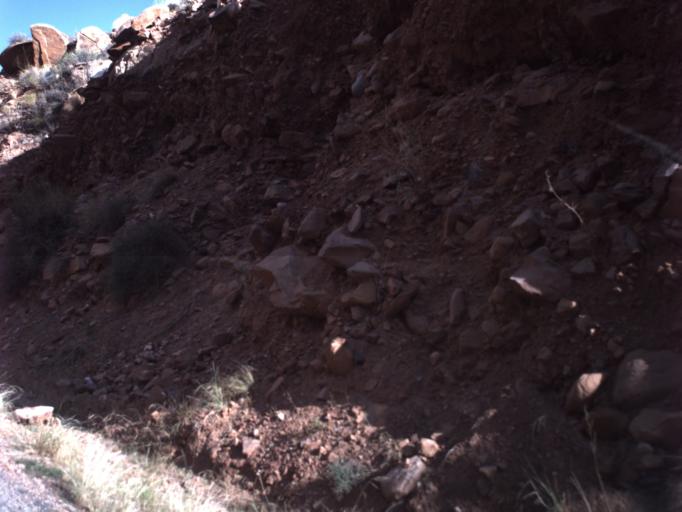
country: US
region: Utah
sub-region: Grand County
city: Moab
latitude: 38.6848
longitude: -109.4627
